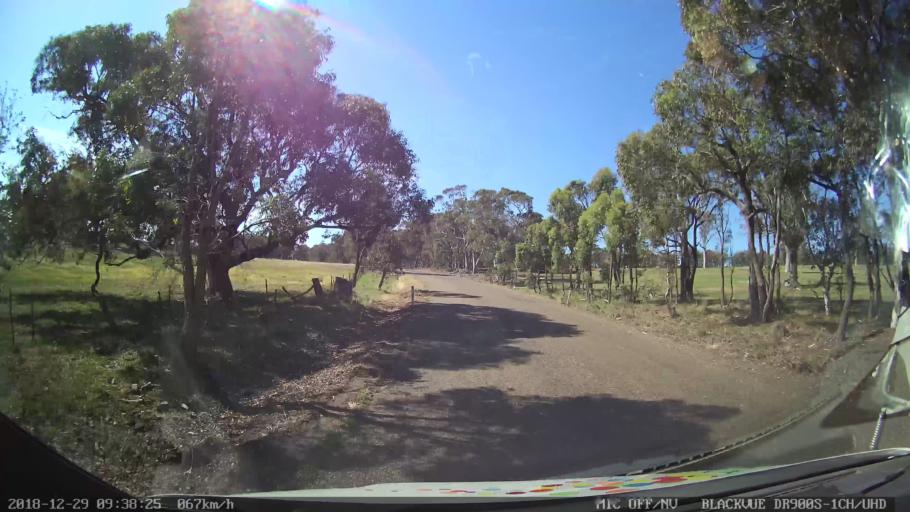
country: AU
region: New South Wales
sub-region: Upper Lachlan Shire
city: Crookwell
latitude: -34.6467
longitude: 149.3762
